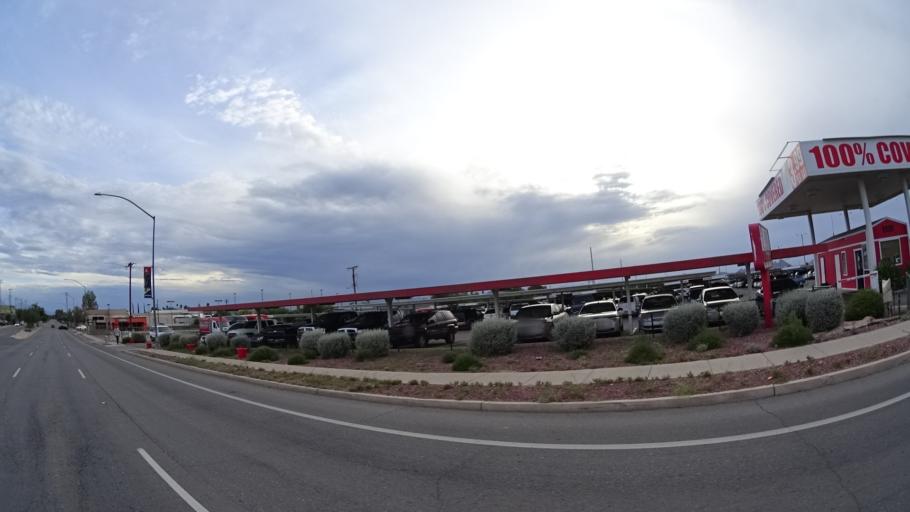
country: US
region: Arizona
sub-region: Pima County
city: Summit
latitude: 32.1328
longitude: -110.9347
